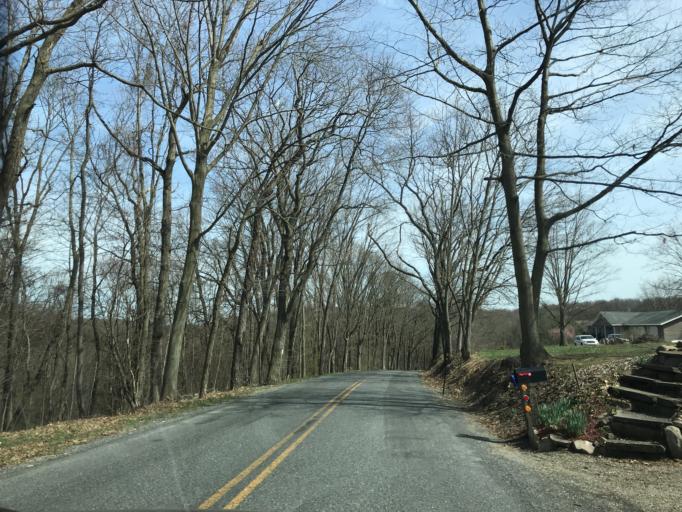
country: US
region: Pennsylvania
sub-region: Northumberland County
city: Northumberland
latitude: 40.8809
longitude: -76.8119
